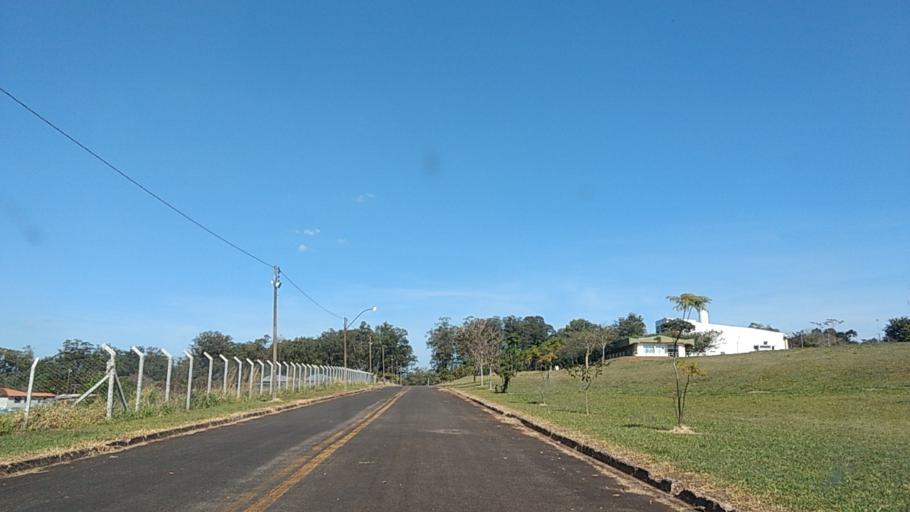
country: BR
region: Sao Paulo
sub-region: Botucatu
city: Botucatu
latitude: -22.8454
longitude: -48.4331
